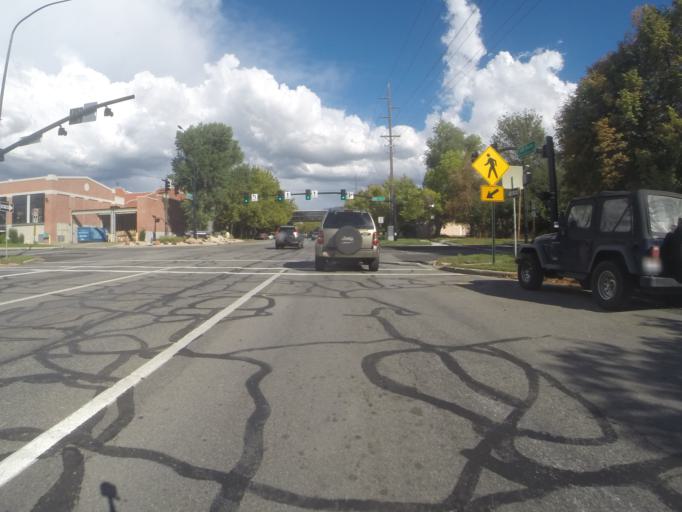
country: US
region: Utah
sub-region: Salt Lake County
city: Salt Lake City
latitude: 40.7563
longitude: -111.8743
